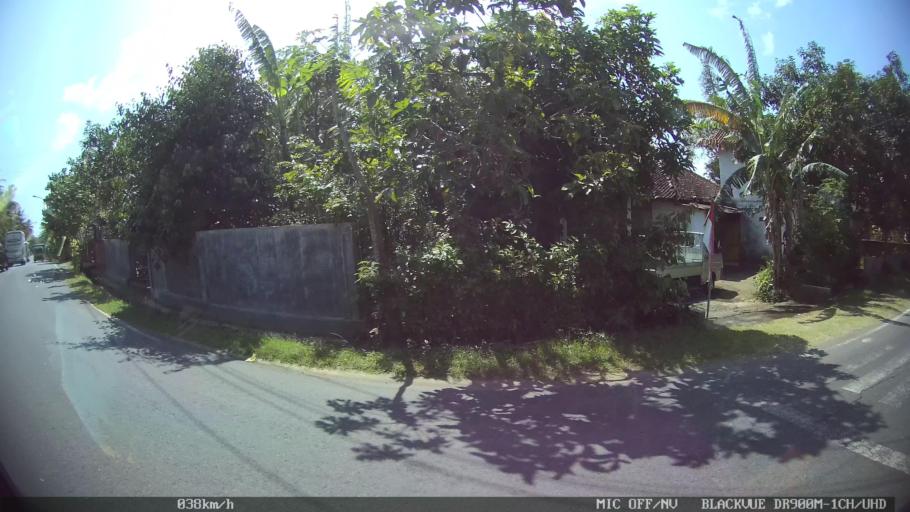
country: ID
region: Daerah Istimewa Yogyakarta
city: Pundong
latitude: -7.9866
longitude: 110.3315
